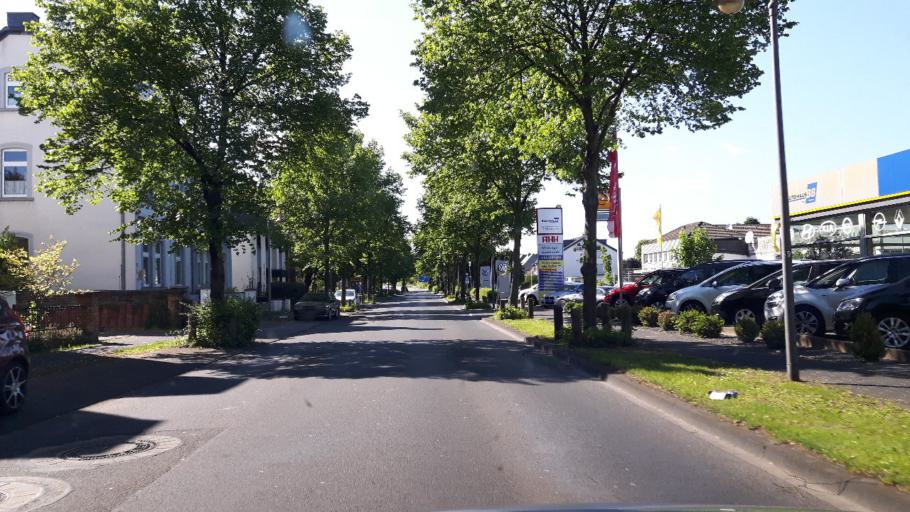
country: DE
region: North Rhine-Westphalia
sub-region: Regierungsbezirk Koln
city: Hennef
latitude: 50.7789
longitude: 7.2750
